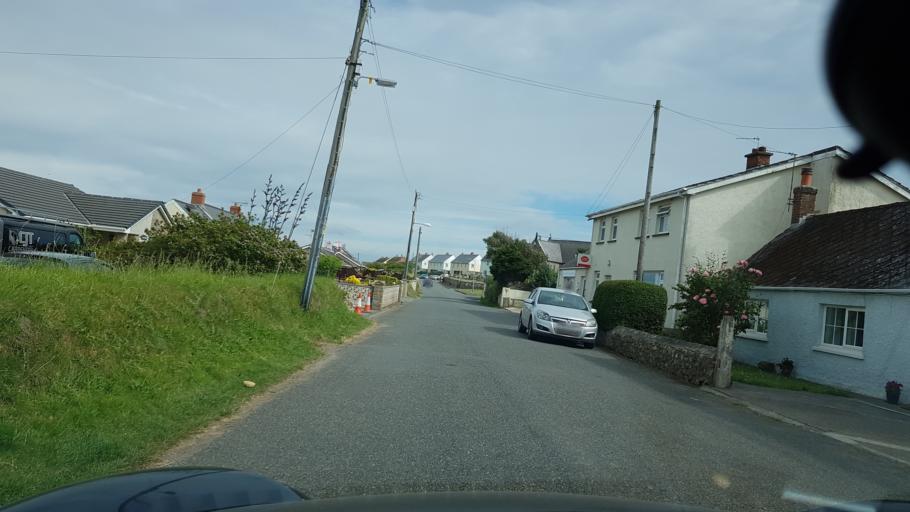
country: GB
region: Wales
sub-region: Pembrokeshire
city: Dale
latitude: 51.7303
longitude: -5.1956
